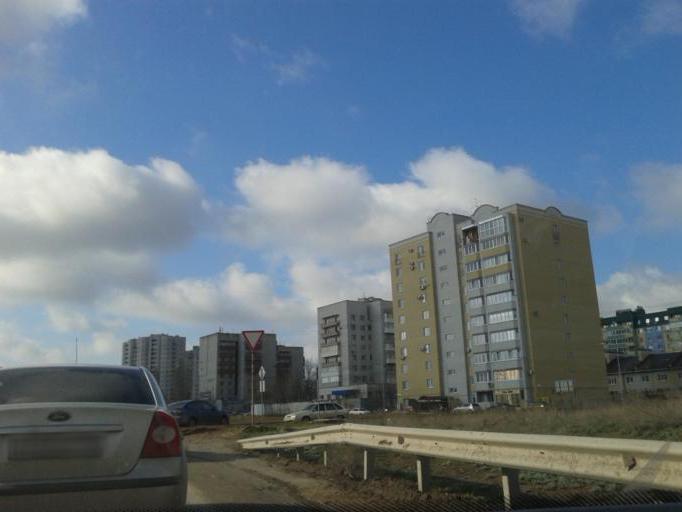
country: RU
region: Volgograd
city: Volgograd
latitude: 48.7622
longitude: 44.4977
